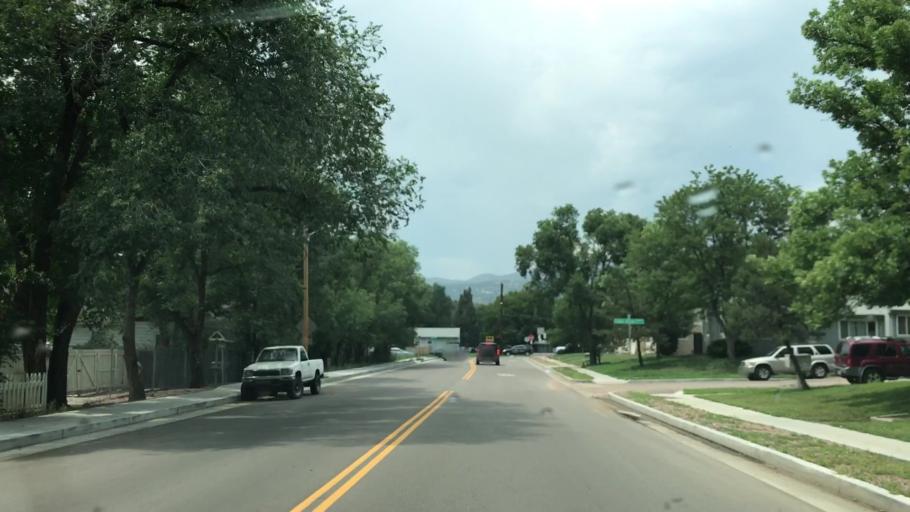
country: US
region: Colorado
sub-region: El Paso County
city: Colorado Springs
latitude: 38.8545
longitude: -104.8656
